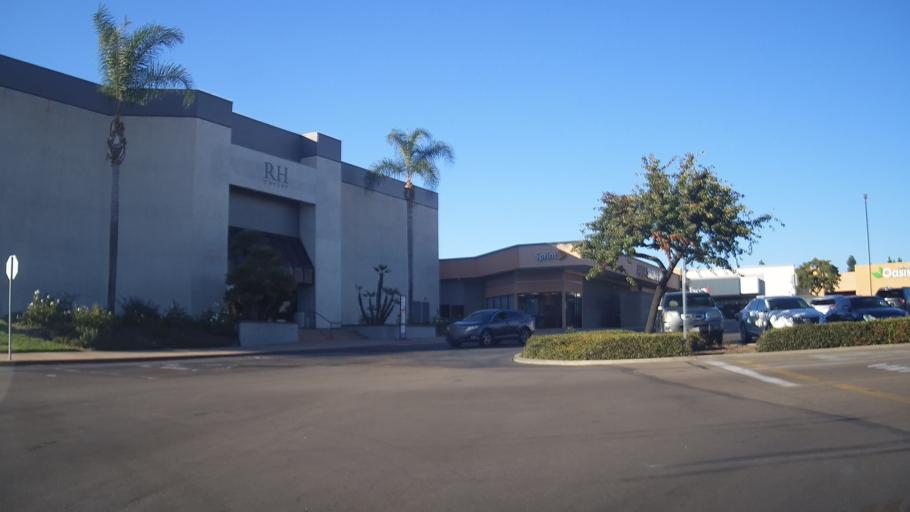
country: US
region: California
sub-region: San Diego County
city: La Mesa
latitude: 32.7767
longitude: -117.0108
